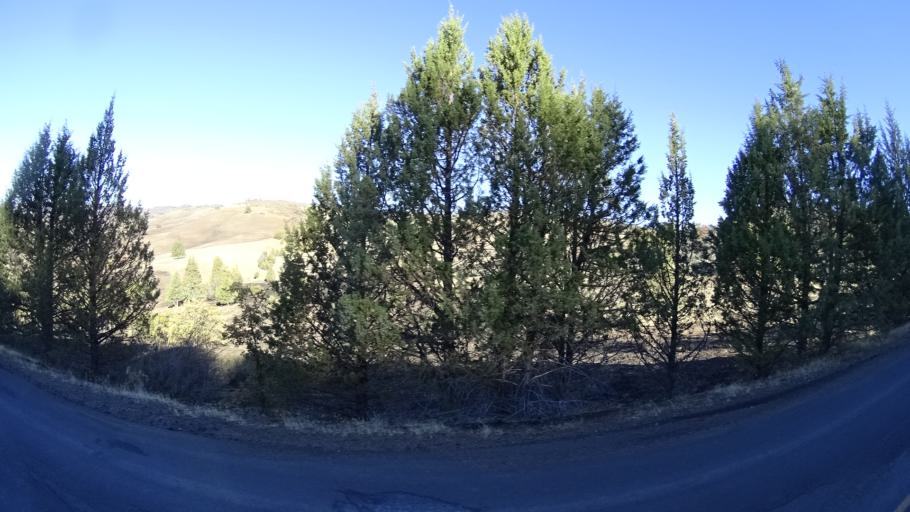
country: US
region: California
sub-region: Siskiyou County
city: Montague
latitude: 41.9428
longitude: -122.4426
